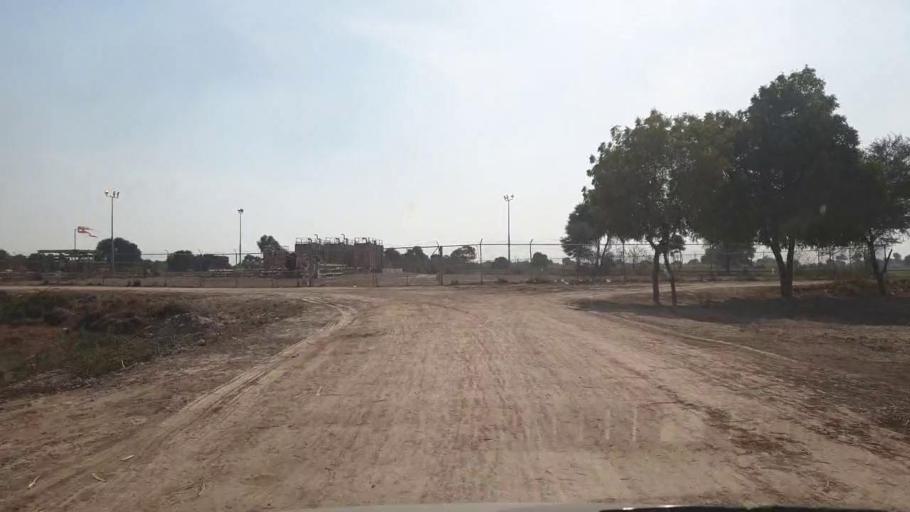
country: PK
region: Sindh
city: Chambar
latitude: 25.3258
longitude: 68.7735
